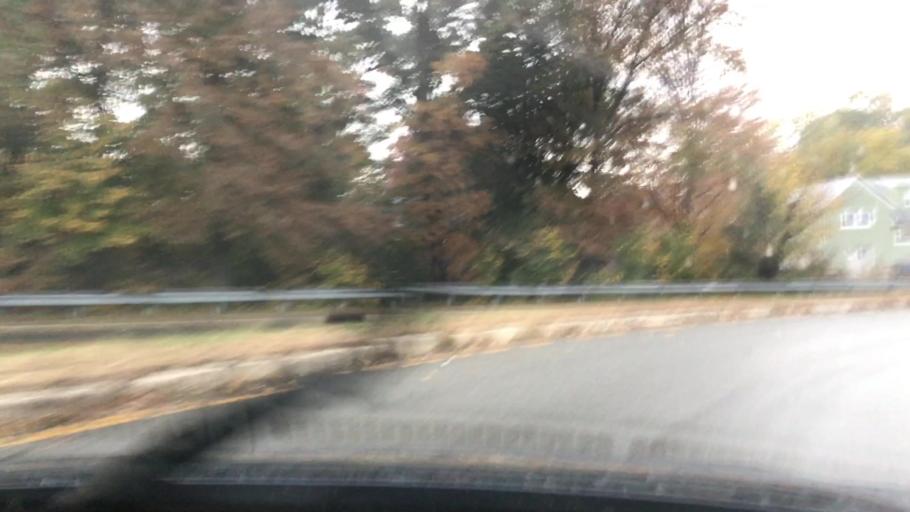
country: US
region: New Jersey
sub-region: Bergen County
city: Hasbrouck Heights
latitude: 40.8714
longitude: -74.0679
